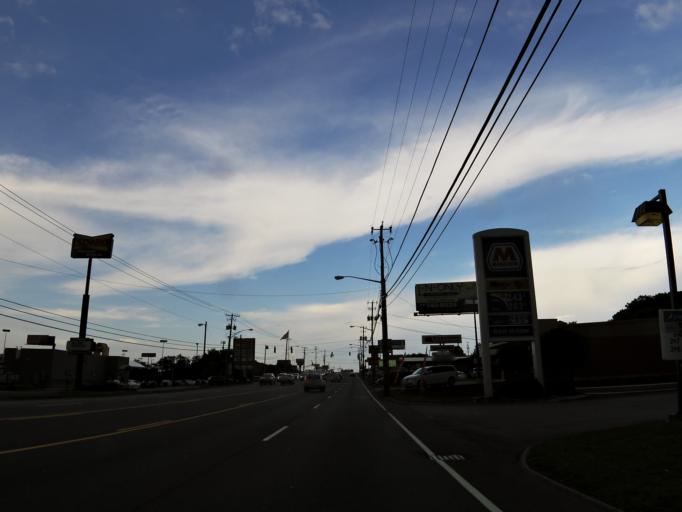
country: US
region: Tennessee
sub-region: Knox County
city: Farragut
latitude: 35.9217
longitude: -84.0636
